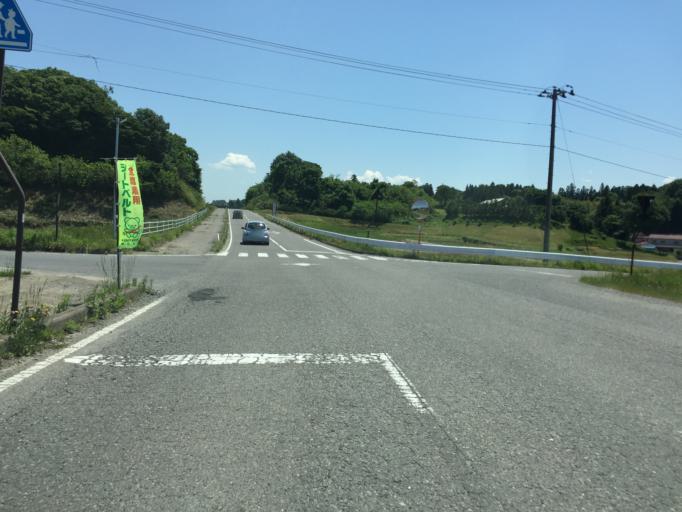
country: JP
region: Fukushima
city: Motomiya
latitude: 37.5281
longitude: 140.4334
